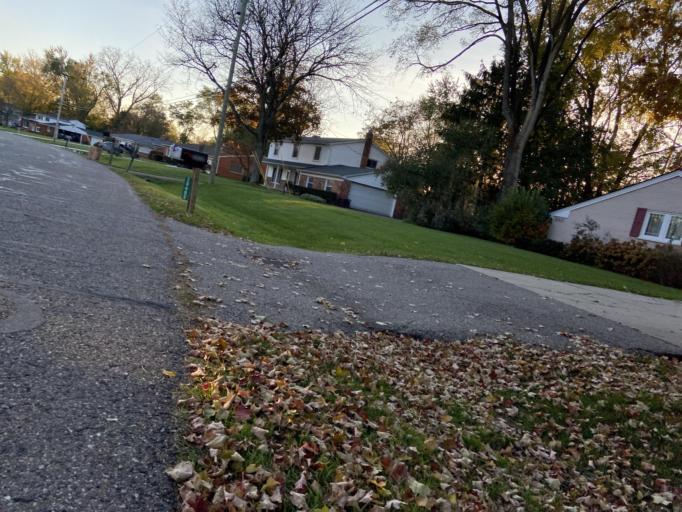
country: US
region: Michigan
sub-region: Oakland County
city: Farmington Hills
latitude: 42.5047
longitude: -83.3709
